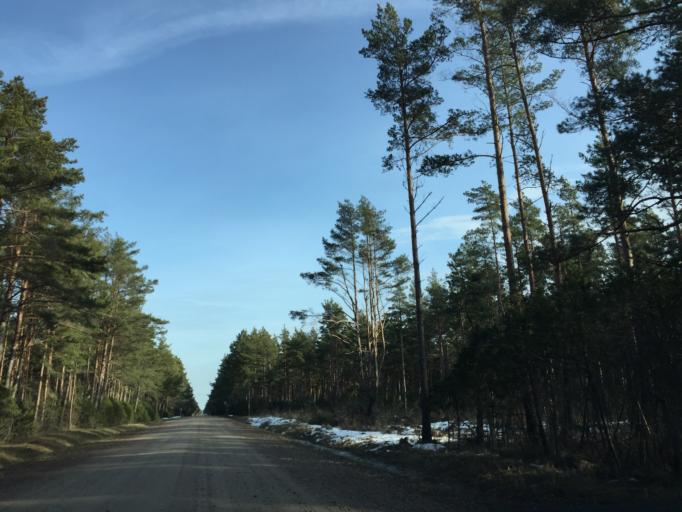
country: EE
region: Saare
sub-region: Kuressaare linn
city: Kuressaare
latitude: 58.2952
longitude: 21.9466
